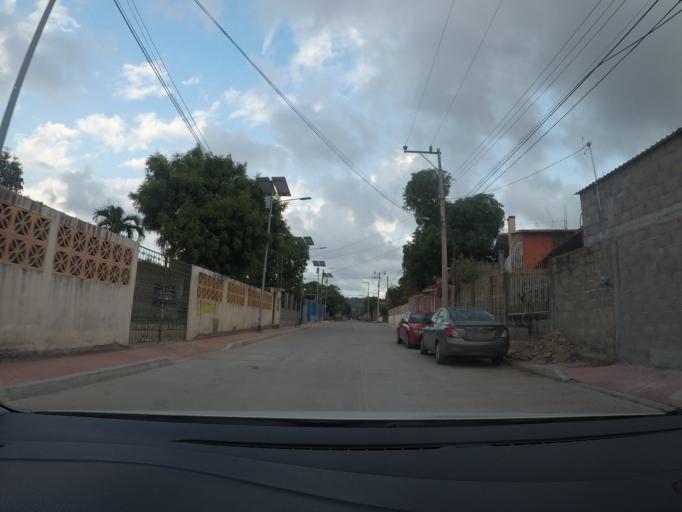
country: MX
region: Oaxaca
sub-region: Salina Cruz
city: Salina Cruz
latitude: 16.2079
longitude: -95.2004
